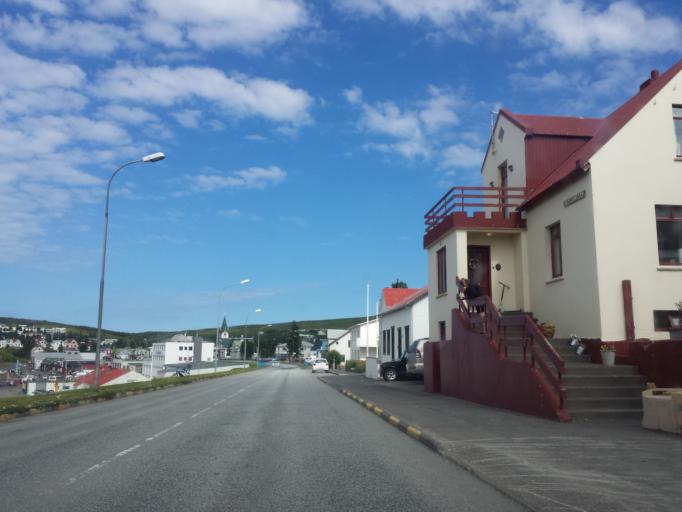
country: IS
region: Northeast
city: Husavik
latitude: 66.0428
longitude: -17.3419
